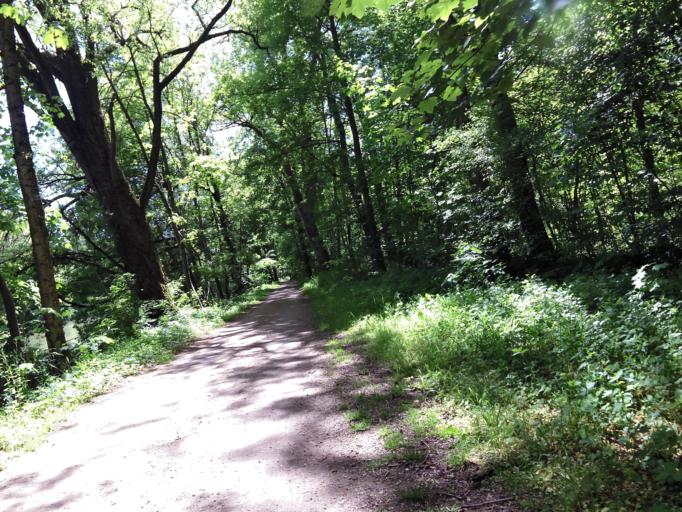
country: DE
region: Bavaria
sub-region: Upper Bavaria
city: Freising
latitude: 48.3923
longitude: 11.7471
